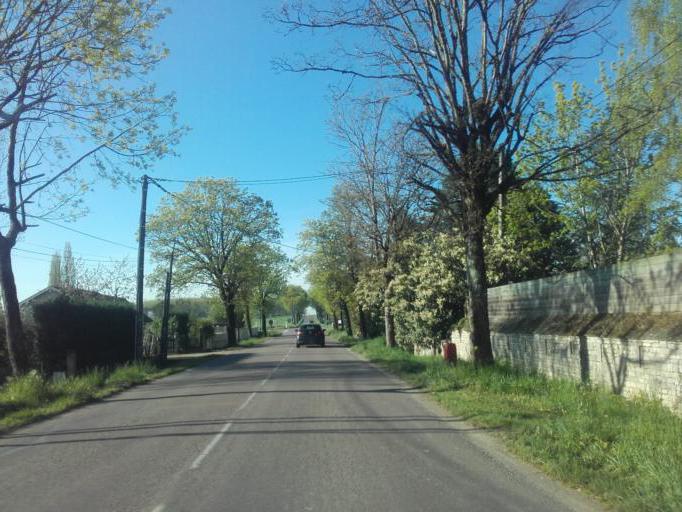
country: FR
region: Bourgogne
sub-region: Departement de Saone-et-Loire
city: Givry
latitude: 46.7690
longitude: 4.7382
